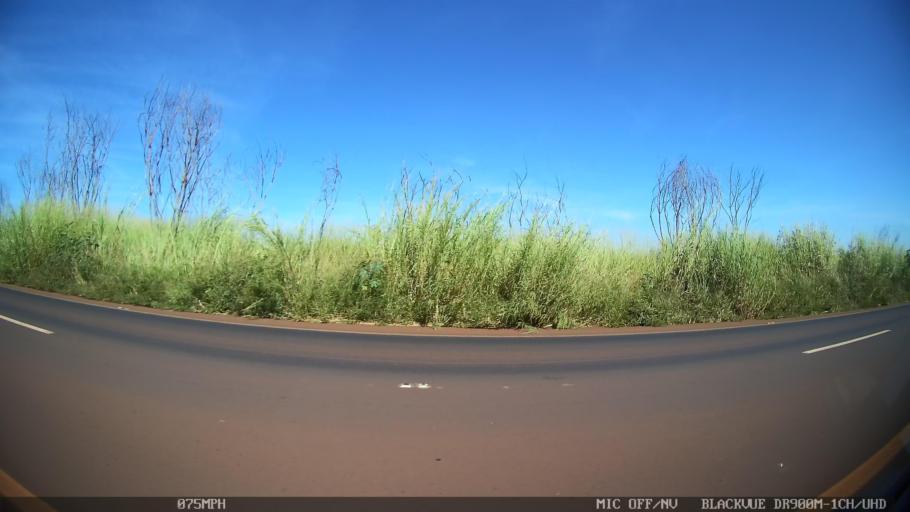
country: BR
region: Sao Paulo
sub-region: Sao Joaquim Da Barra
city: Sao Joaquim da Barra
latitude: -20.5430
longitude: -47.7945
